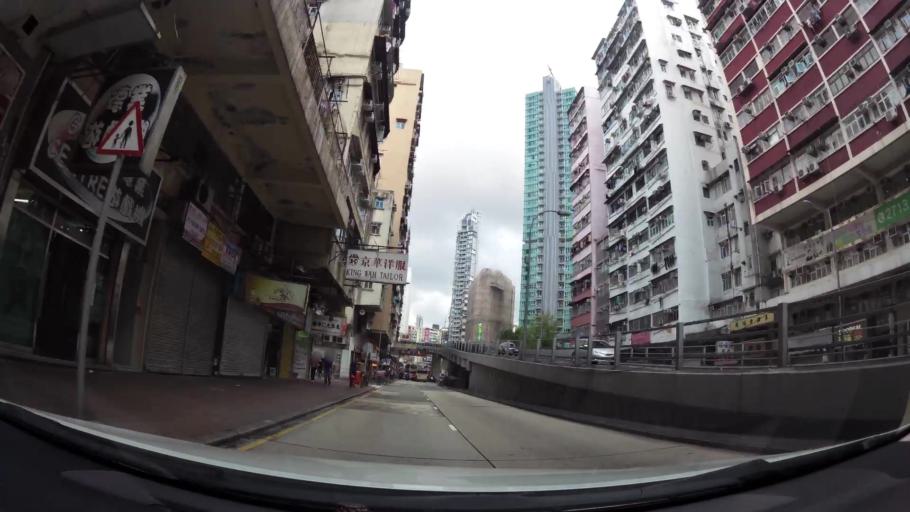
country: HK
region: Sham Shui Po
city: Sham Shui Po
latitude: 22.3247
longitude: 114.1657
